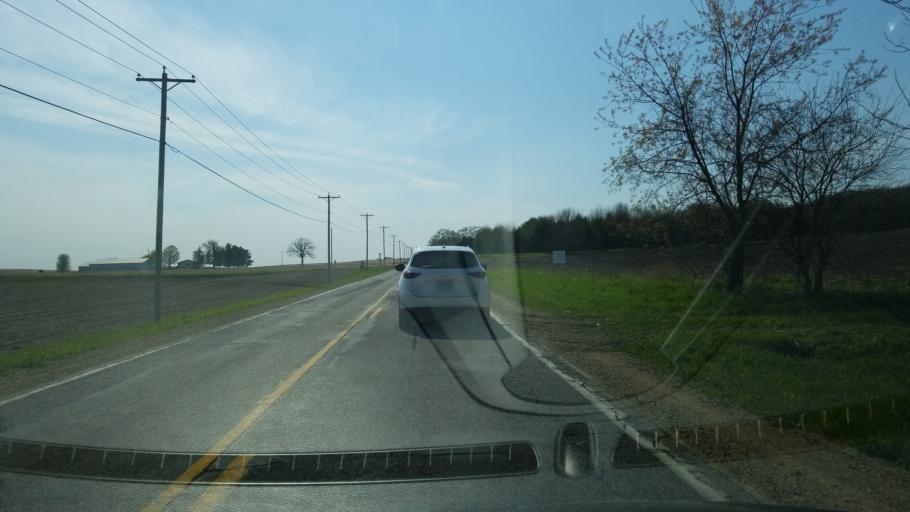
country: US
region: Wisconsin
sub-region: Dane County
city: Oregon
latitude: 42.9291
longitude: -89.4110
